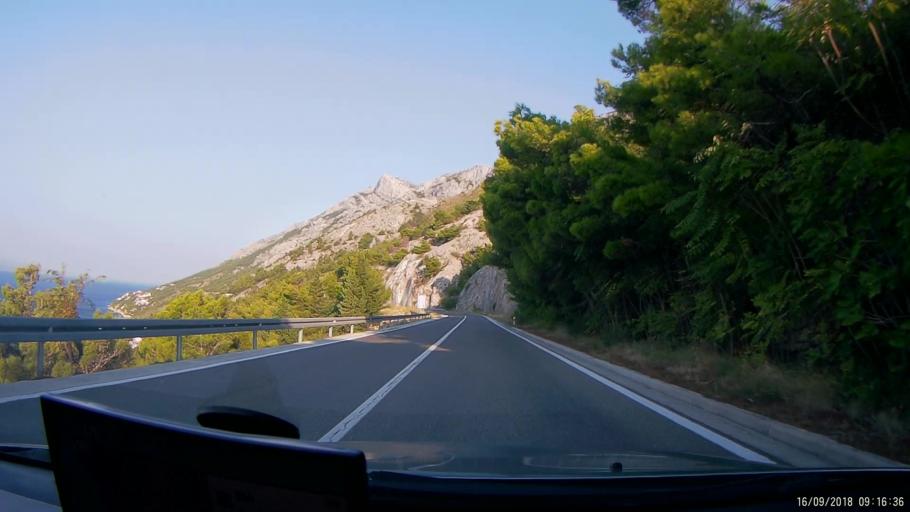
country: HR
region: Splitsko-Dalmatinska
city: Donja Brela
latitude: 43.4010
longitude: 16.8654
